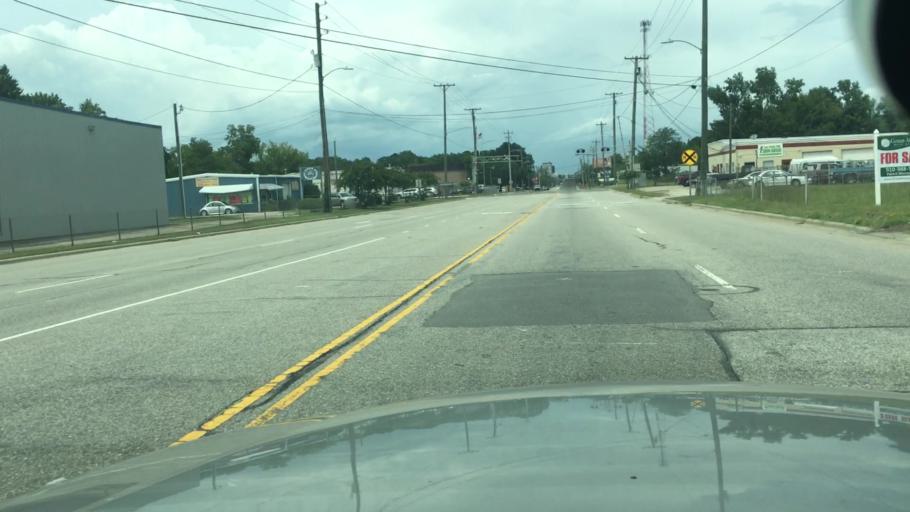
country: US
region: North Carolina
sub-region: Cumberland County
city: Fayetteville
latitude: 35.0389
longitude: -78.8830
